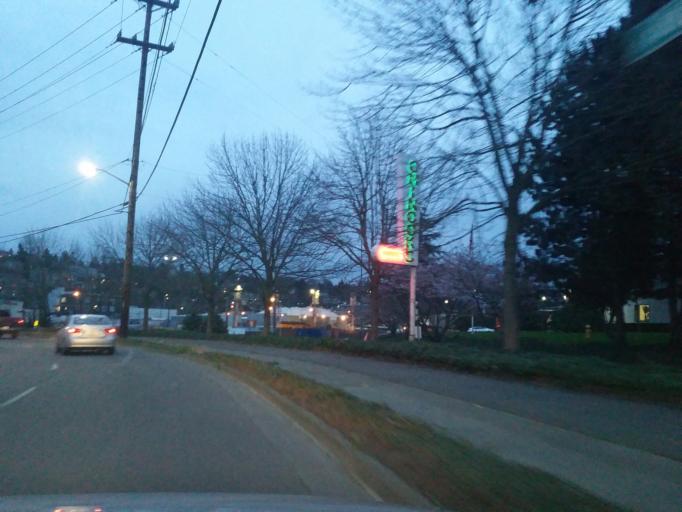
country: US
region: Washington
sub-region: King County
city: Seattle
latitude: 47.6543
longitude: -122.3813
